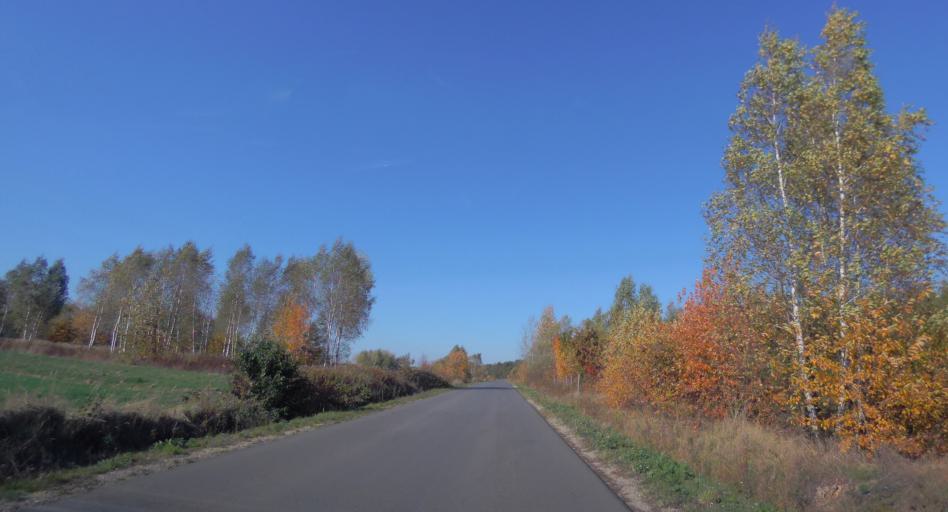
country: PL
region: Subcarpathian Voivodeship
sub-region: Powiat lezajski
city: Wola Zarczycka
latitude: 50.2863
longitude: 22.2726
